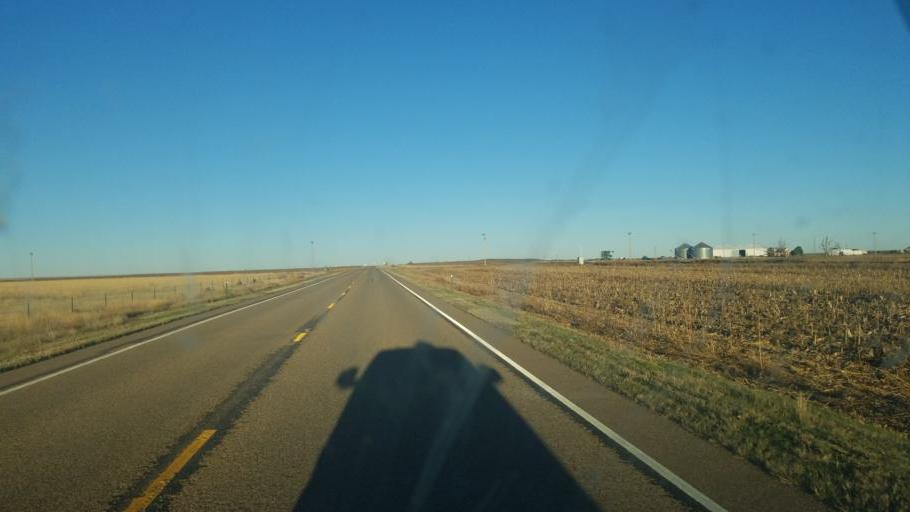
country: US
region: Colorado
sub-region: Cheyenne County
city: Cheyenne Wells
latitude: 38.8104
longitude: -102.4599
